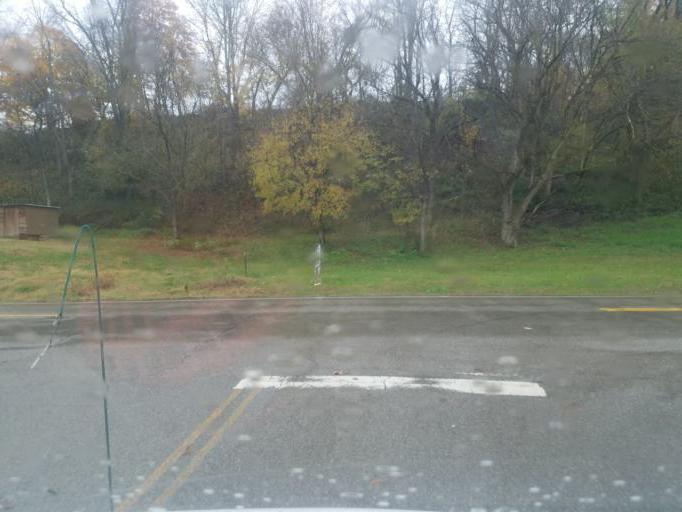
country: US
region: Ohio
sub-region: Washington County
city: Beverly
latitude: 39.4652
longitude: -81.6280
